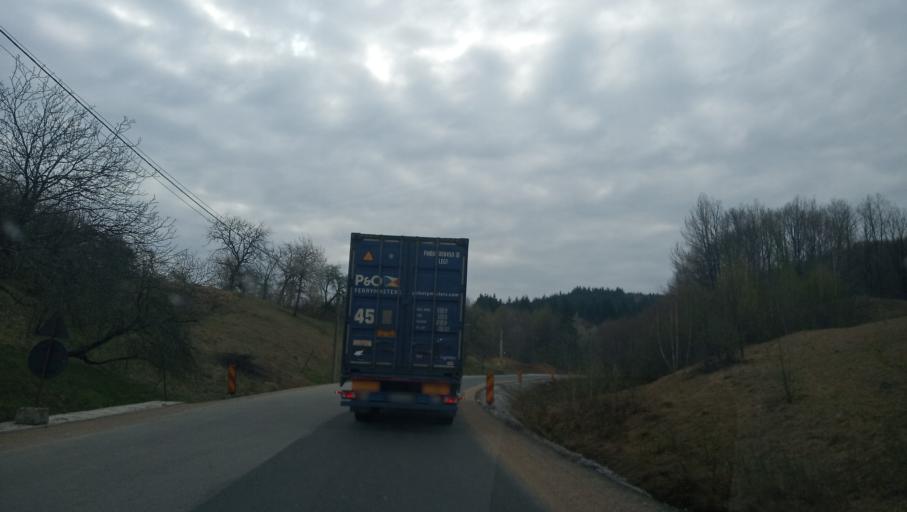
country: RO
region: Bihor
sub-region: Comuna Cristioru de Jos
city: Cristioru de Jos
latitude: 46.4161
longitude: 22.5369
